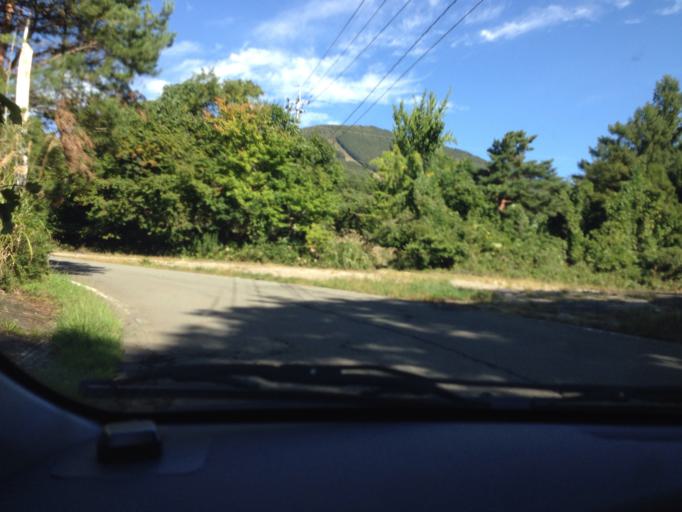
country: JP
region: Fukushima
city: Inawashiro
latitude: 37.5725
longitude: 140.0978
